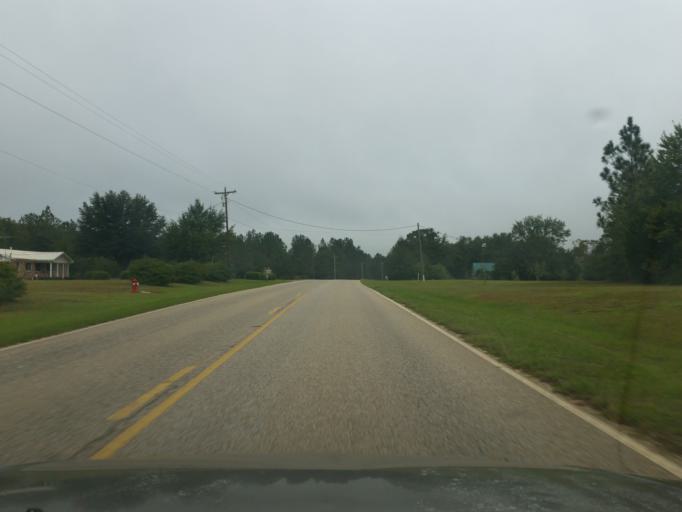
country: US
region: Florida
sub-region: Escambia County
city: Cantonment
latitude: 30.6415
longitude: -87.4449
